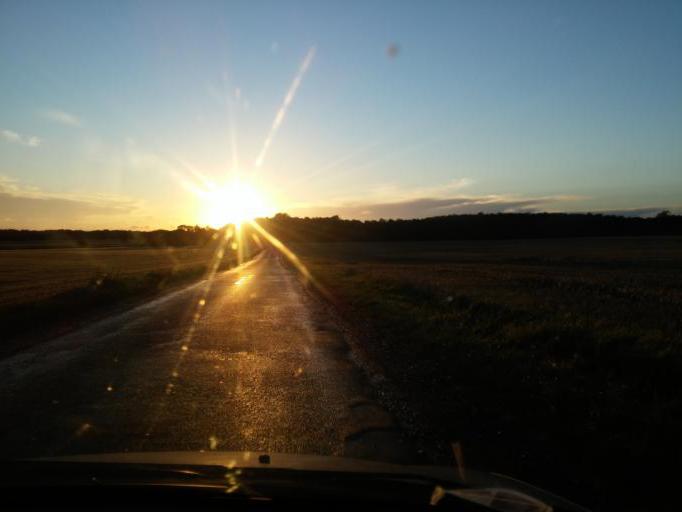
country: DK
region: South Denmark
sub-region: Kerteminde Kommune
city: Munkebo
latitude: 55.4239
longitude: 10.5637
